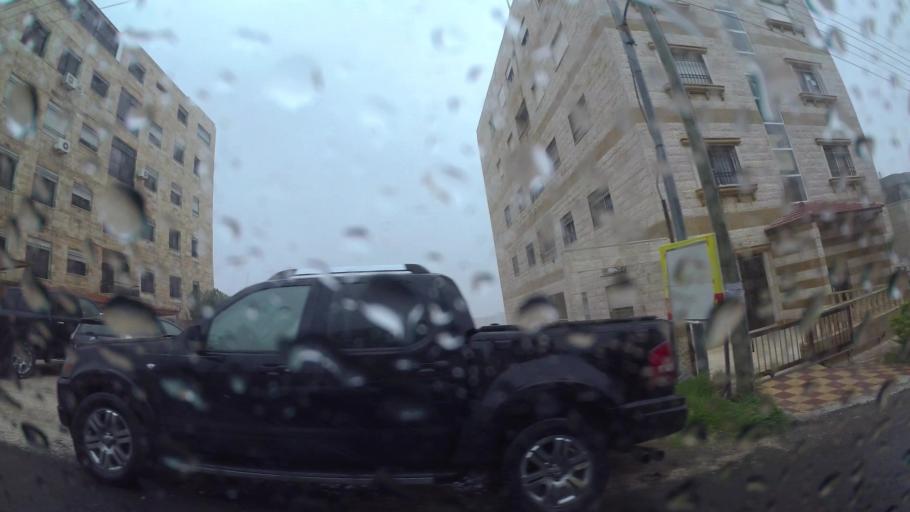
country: JO
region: Amman
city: Al Jubayhah
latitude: 32.0427
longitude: 35.8941
